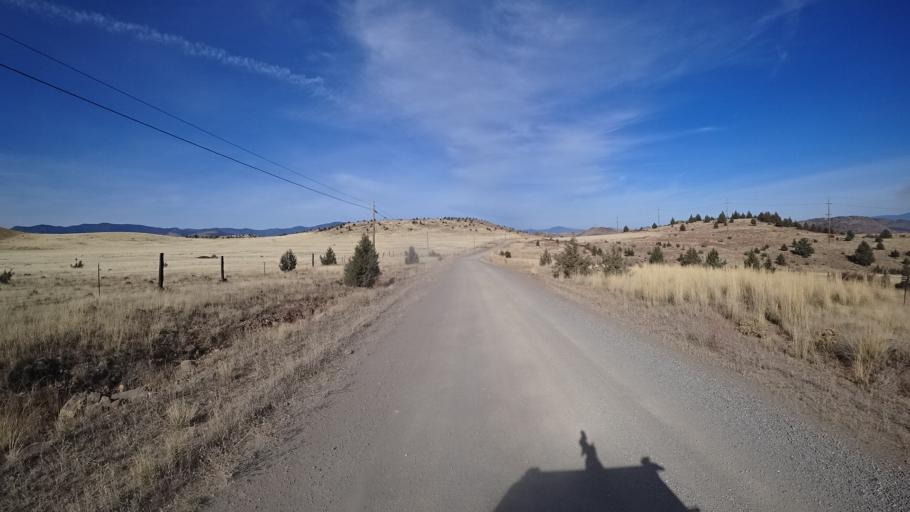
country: US
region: California
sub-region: Siskiyou County
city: Weed
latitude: 41.4938
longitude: -122.4533
